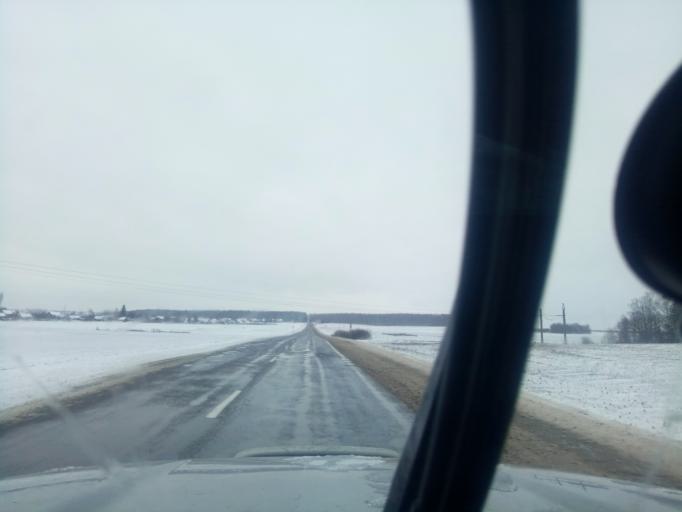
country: BY
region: Minsk
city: Kapyl'
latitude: 53.1178
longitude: 27.0669
